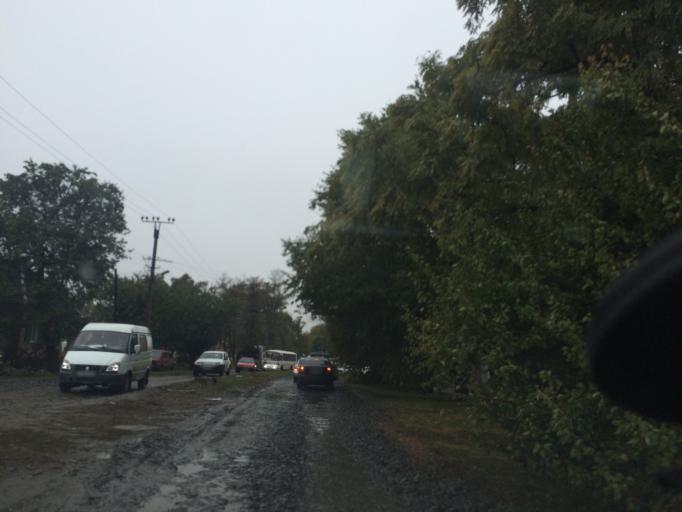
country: RU
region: Rostov
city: Azov
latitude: 47.1046
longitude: 39.4317
